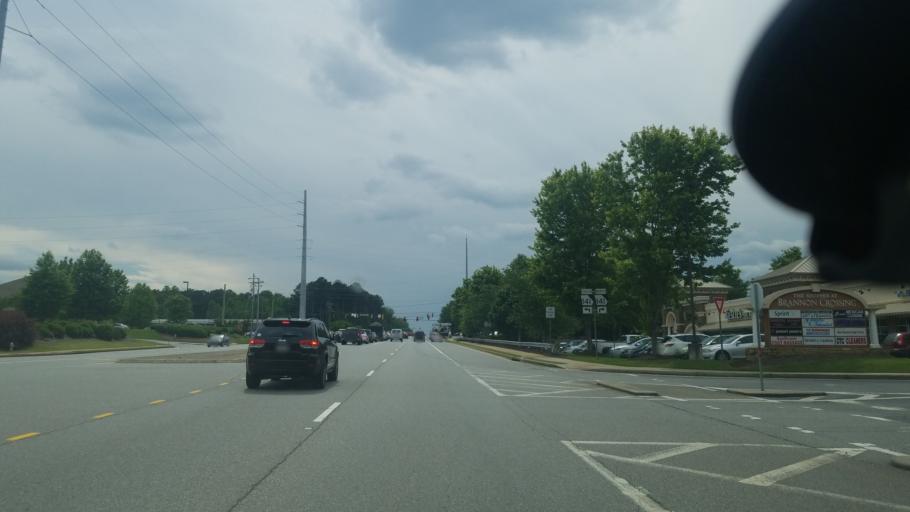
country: US
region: Georgia
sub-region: Forsyth County
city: Cumming
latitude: 34.1515
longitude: -84.1715
